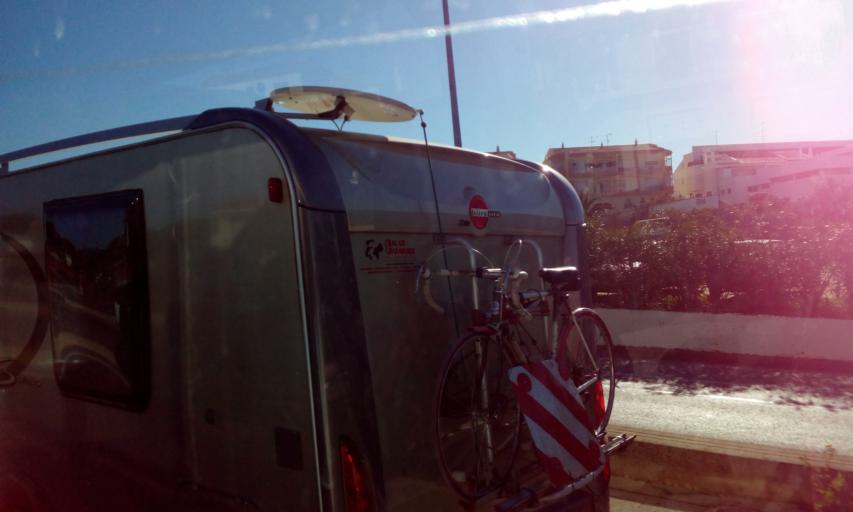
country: PT
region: Faro
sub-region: Faro
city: Faro
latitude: 37.0341
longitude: -7.9623
